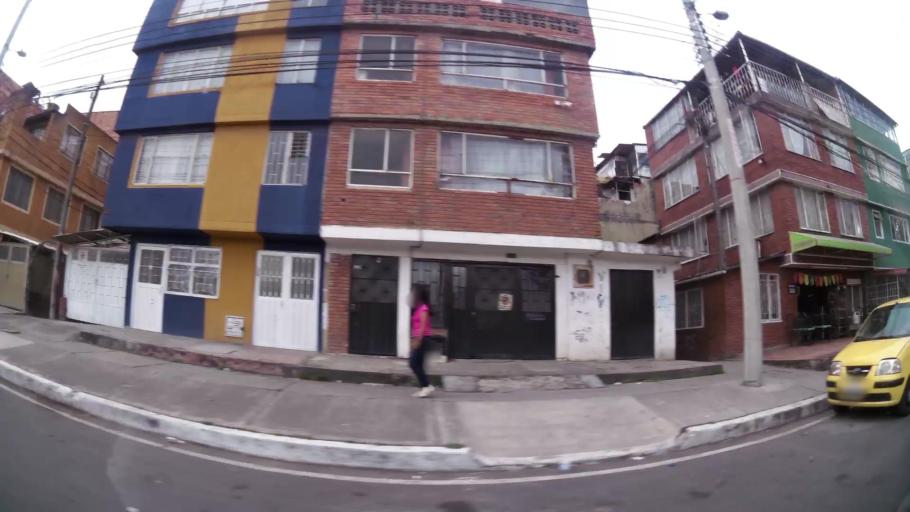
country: CO
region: Cundinamarca
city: Cota
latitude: 4.7176
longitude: -74.1021
